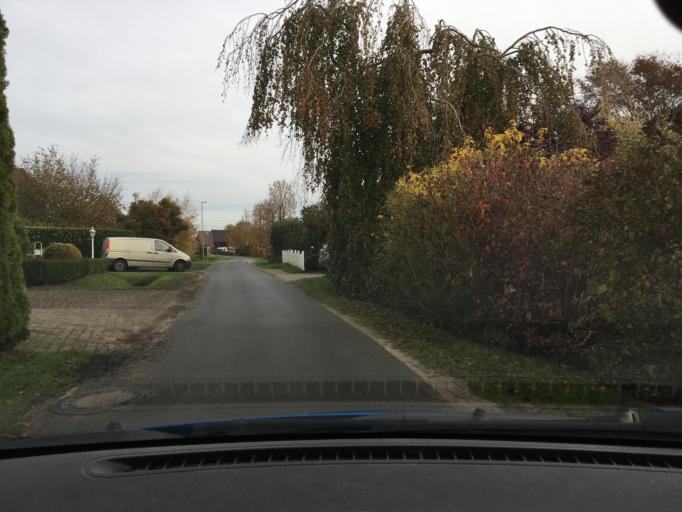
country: DE
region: Lower Saxony
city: Bardowick
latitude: 53.3123
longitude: 10.3827
